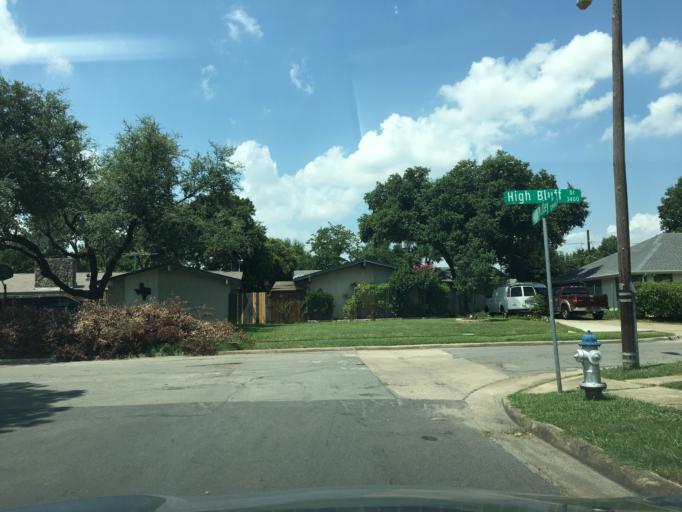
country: US
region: Texas
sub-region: Dallas County
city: Farmers Branch
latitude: 32.9130
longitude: -96.8650
